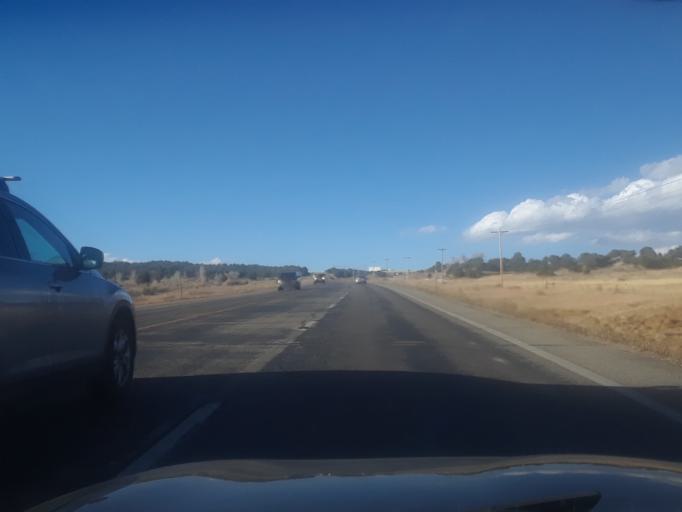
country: US
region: Colorado
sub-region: Chaffee County
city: Salida
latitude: 38.6480
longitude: -106.0843
